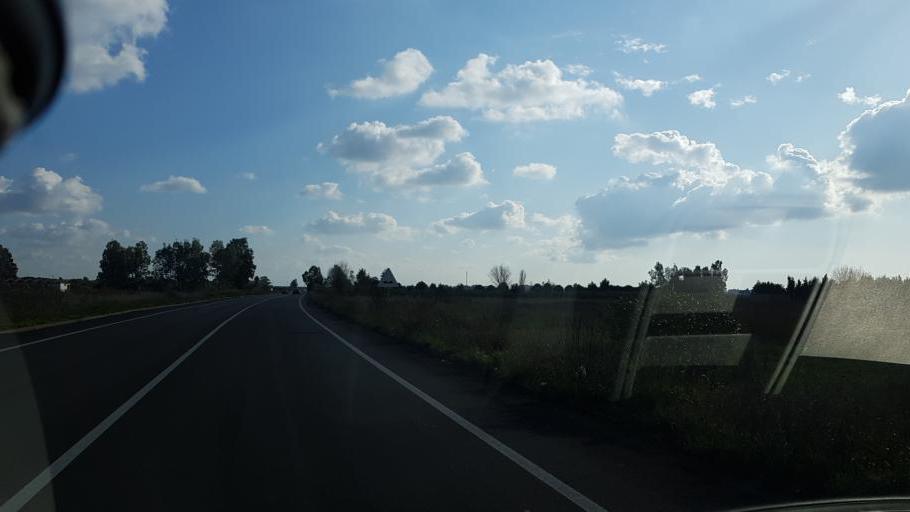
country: IT
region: Apulia
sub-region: Provincia di Lecce
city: Veglie
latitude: 40.3459
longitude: 17.9752
